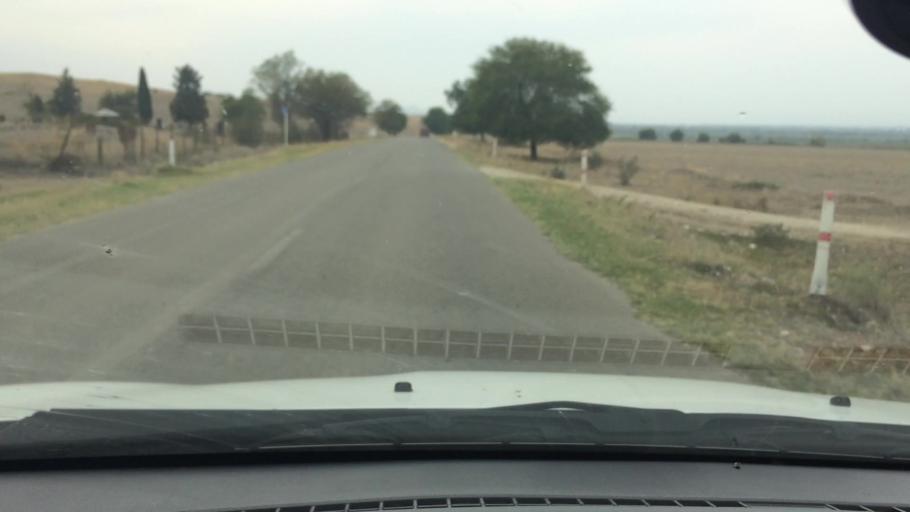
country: AM
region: Tavush
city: Berdavan
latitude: 41.3372
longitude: 45.0121
